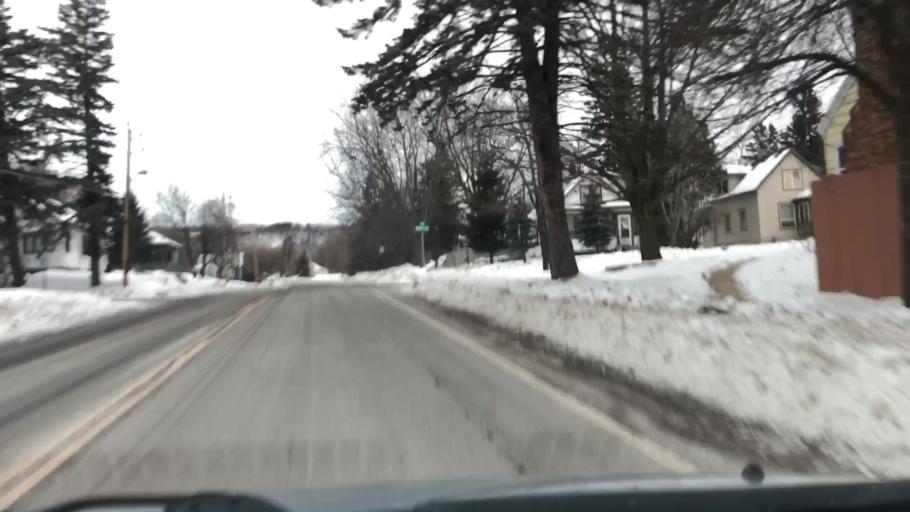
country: US
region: Minnesota
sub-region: Saint Louis County
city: Arnold
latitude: 46.8340
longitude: -92.0368
